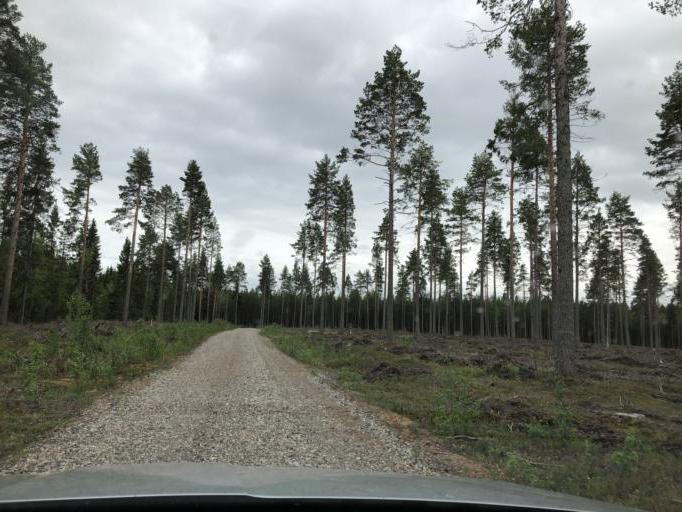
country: SE
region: Norrbotten
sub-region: Pitea Kommun
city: Roknas
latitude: 65.3984
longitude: 21.2697
